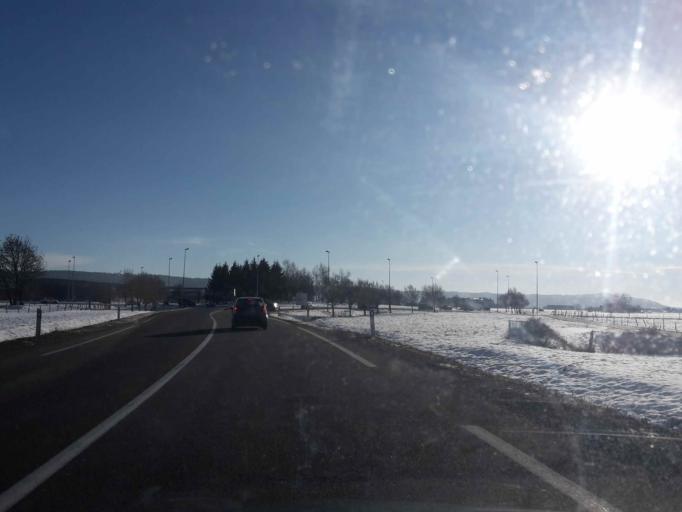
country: FR
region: Franche-Comte
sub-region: Departement du Doubs
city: Doubs
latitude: 46.9264
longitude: 6.3381
